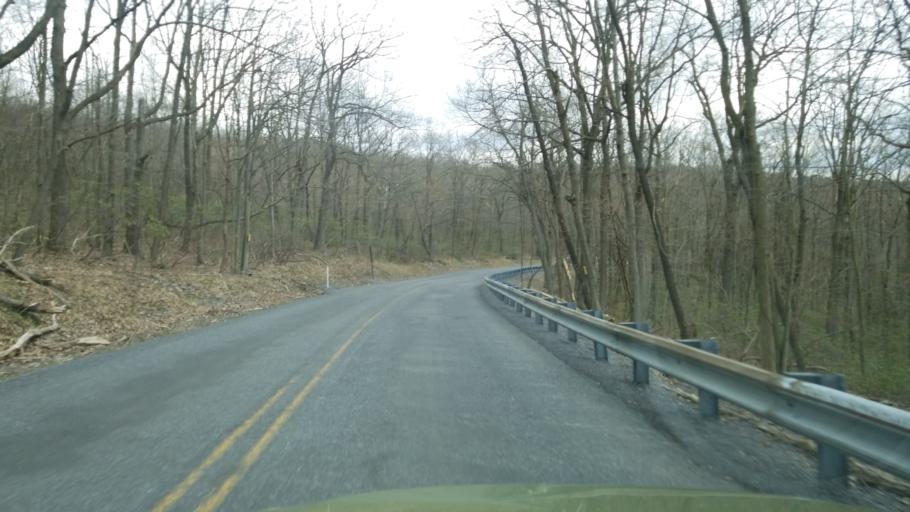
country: US
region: Pennsylvania
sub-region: Blair County
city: Tipton
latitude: 40.7200
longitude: -78.3492
